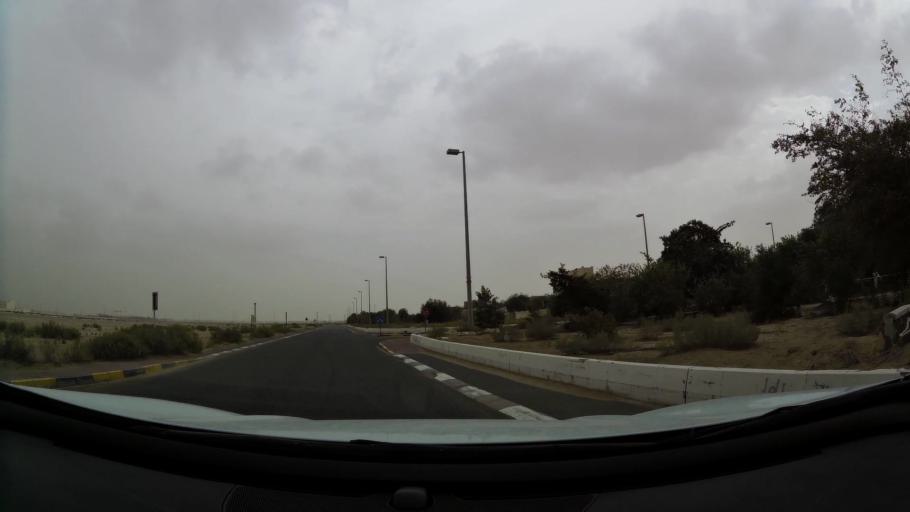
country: AE
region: Abu Dhabi
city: Abu Dhabi
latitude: 24.3708
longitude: 54.6657
